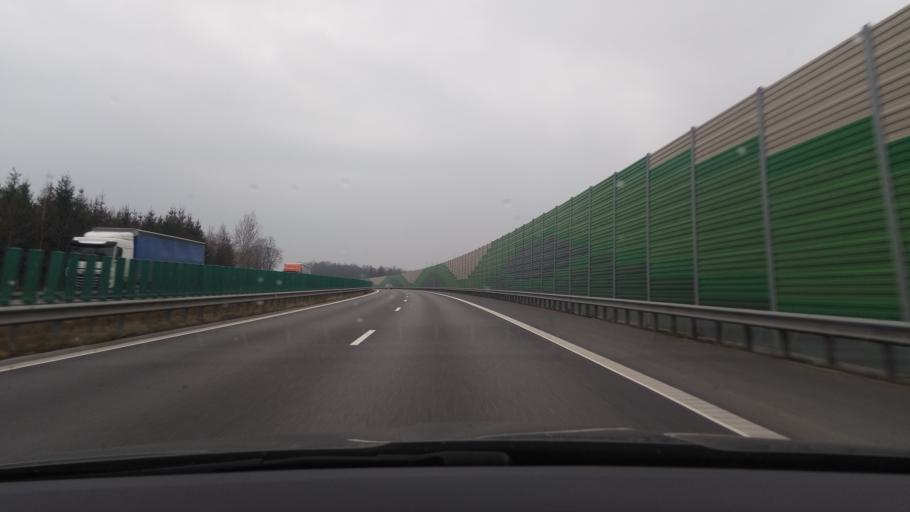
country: LT
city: Kazlu Ruda
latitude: 54.6715
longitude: 23.5264
